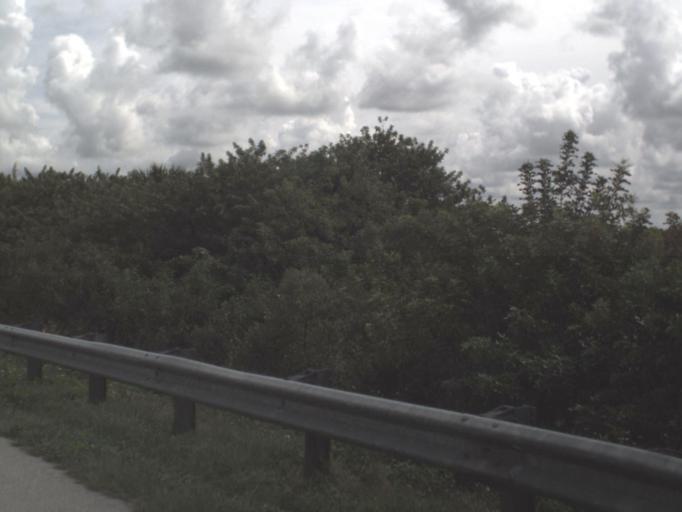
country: US
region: Florida
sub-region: Glades County
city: Buckhead Ridge
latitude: 27.2314
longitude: -81.0858
